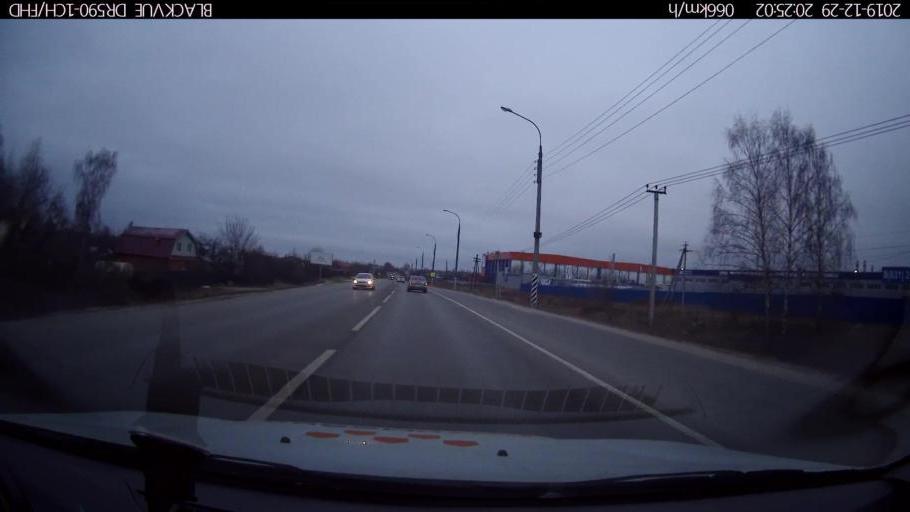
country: RU
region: Nizjnij Novgorod
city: Afonino
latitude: 56.2095
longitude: 44.1095
